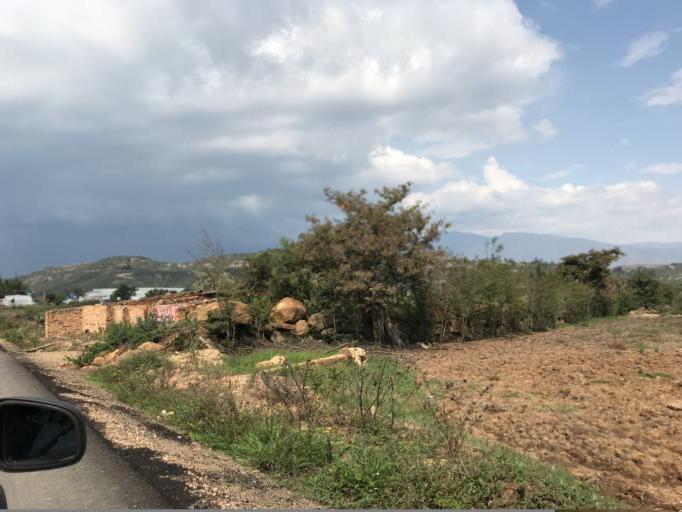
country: CO
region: Boyaca
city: Sutamarchan
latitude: 5.6350
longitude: -73.6007
